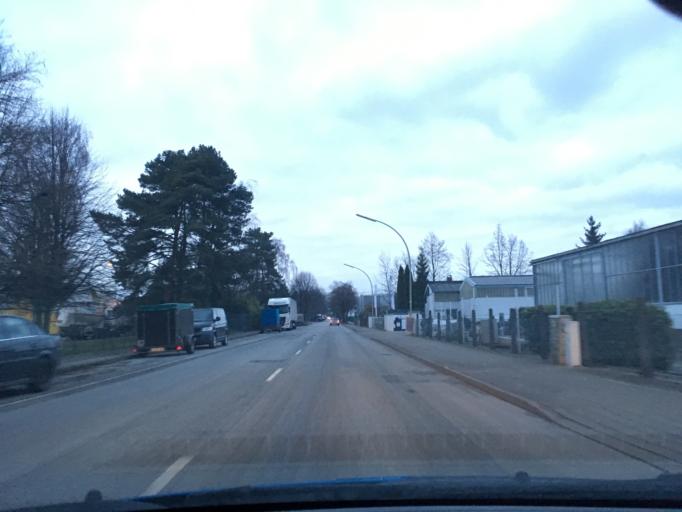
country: DE
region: Schleswig-Holstein
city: Wedel
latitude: 53.5724
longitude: 9.7307
